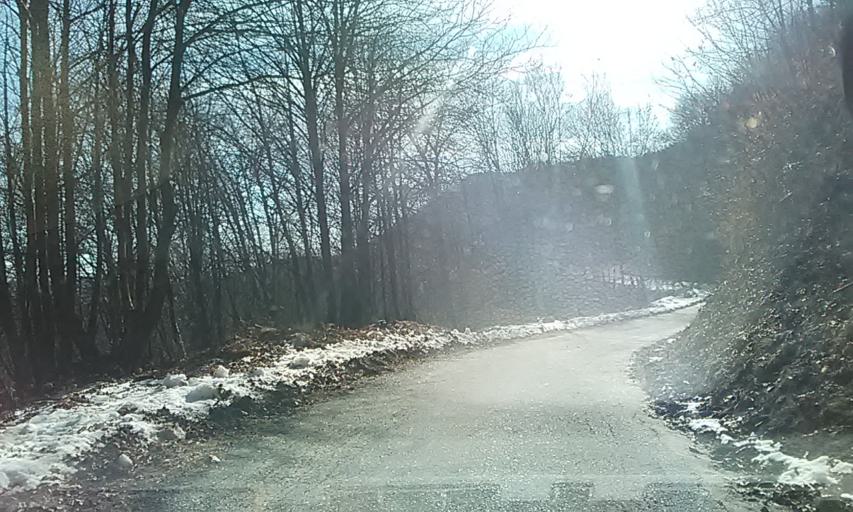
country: IT
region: Piedmont
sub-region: Provincia di Vercelli
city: Cellio
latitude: 45.7701
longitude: 8.3319
